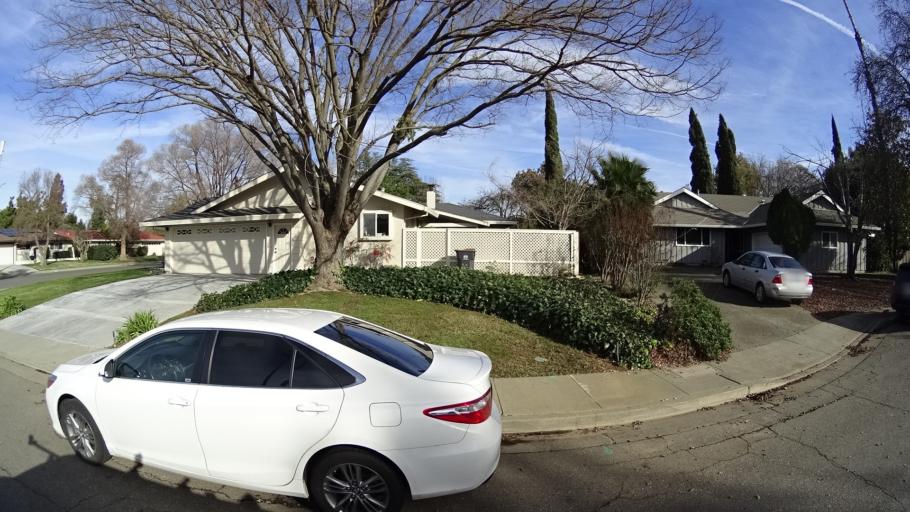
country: US
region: California
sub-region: Yolo County
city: Davis
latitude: 38.5465
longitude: -121.6966
